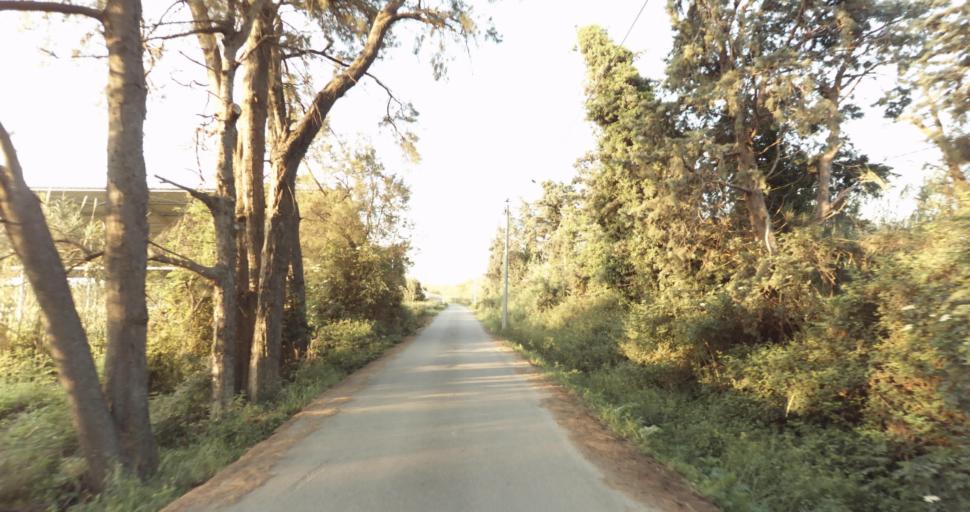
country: FR
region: Corsica
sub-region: Departement de la Haute-Corse
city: Biguglia
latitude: 42.6162
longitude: 9.4457
